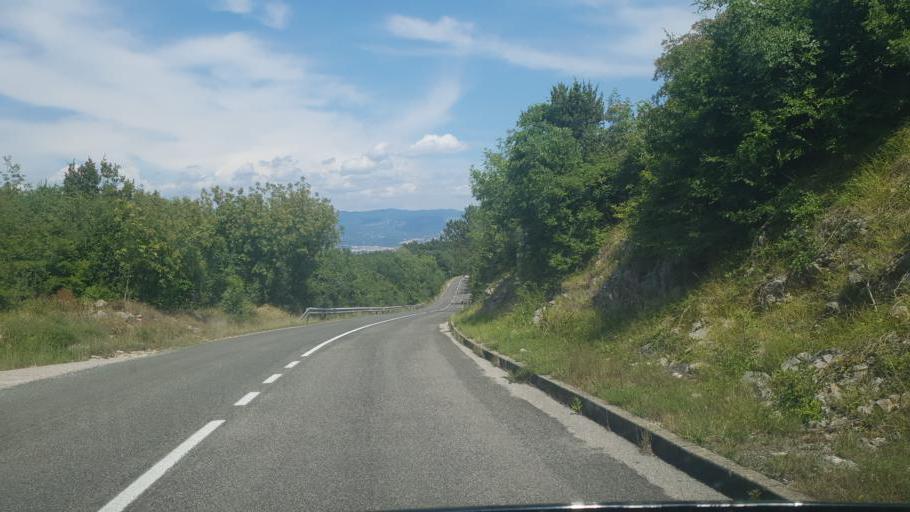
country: HR
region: Primorsko-Goranska
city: Njivice
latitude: 45.1451
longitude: 14.5842
